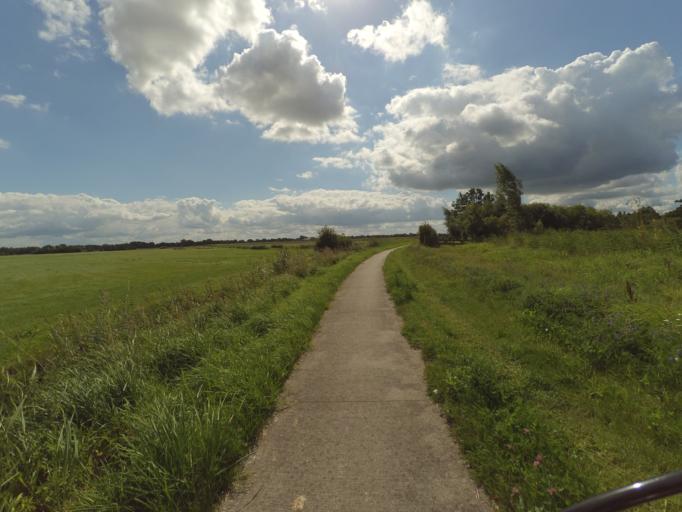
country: NL
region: Friesland
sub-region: Gemeente Tytsjerksteradiel
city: Eastermar
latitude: 53.2048
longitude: 6.0547
